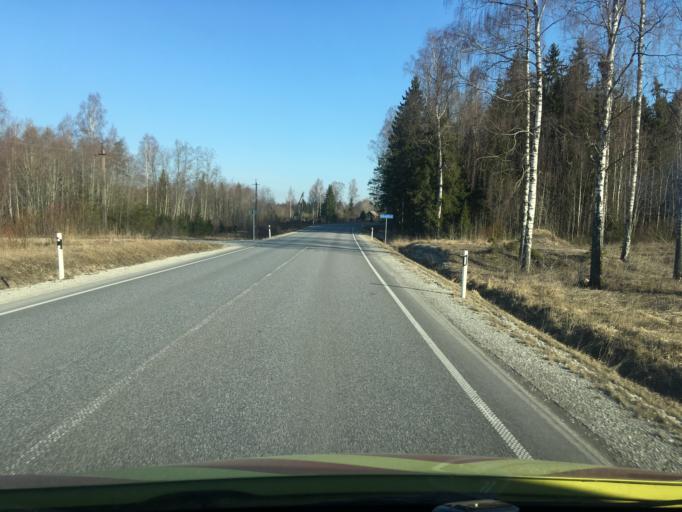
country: EE
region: Raplamaa
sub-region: Rapla vald
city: Rapla
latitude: 59.0104
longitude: 24.8379
